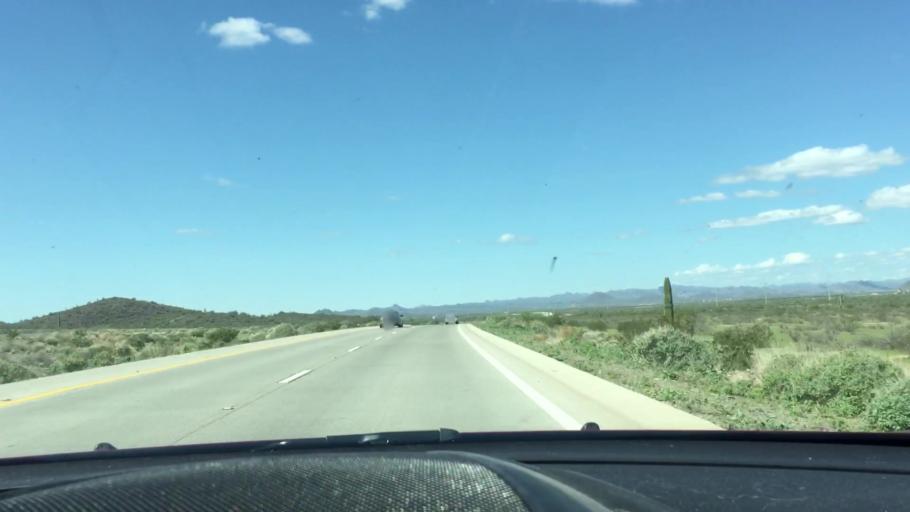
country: US
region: Arizona
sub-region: Maricopa County
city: Anthem
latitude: 33.7716
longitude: -112.1735
